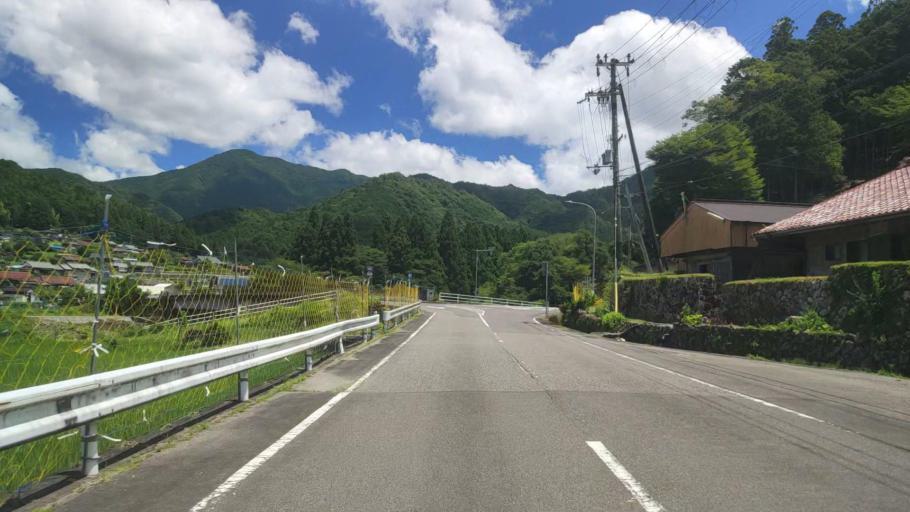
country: JP
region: Mie
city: Owase
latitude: 33.9824
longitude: 136.0392
